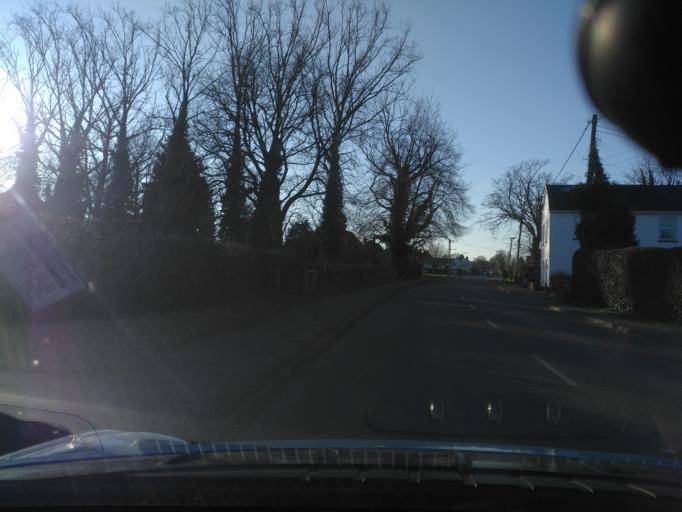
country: GB
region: England
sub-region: Central Bedfordshire
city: Kensworth
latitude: 51.8504
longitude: -0.4981
